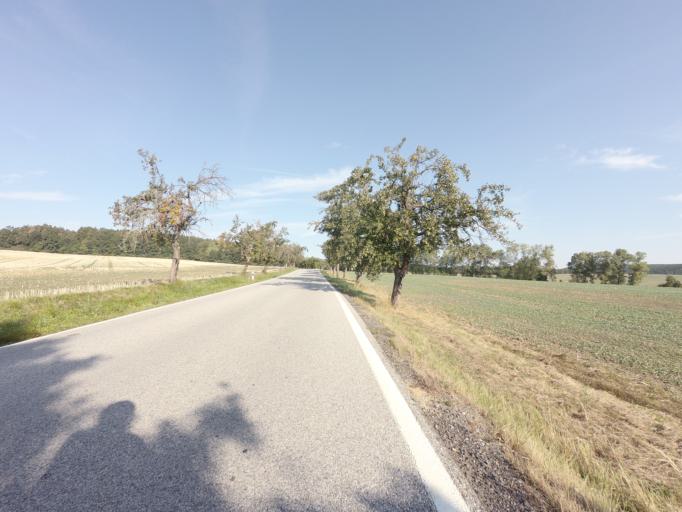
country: CZ
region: Jihocesky
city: Tyn nad Vltavou
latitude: 49.2571
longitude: 14.4168
